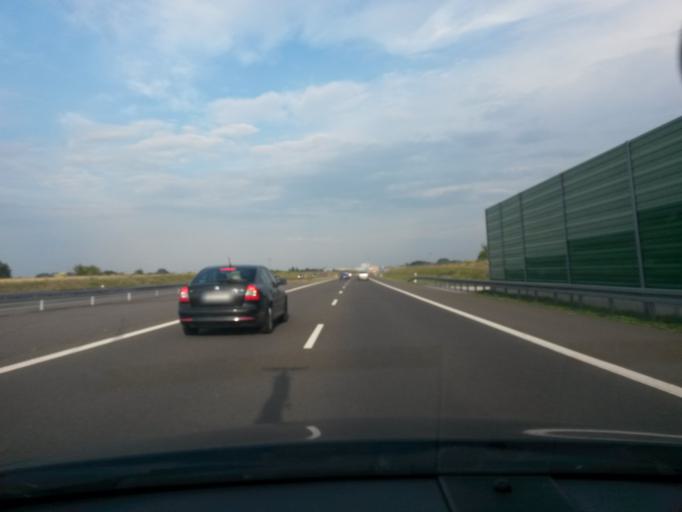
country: PL
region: Lodz Voivodeship
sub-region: Powiat zgierski
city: Strykow
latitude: 51.8971
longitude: 19.5317
